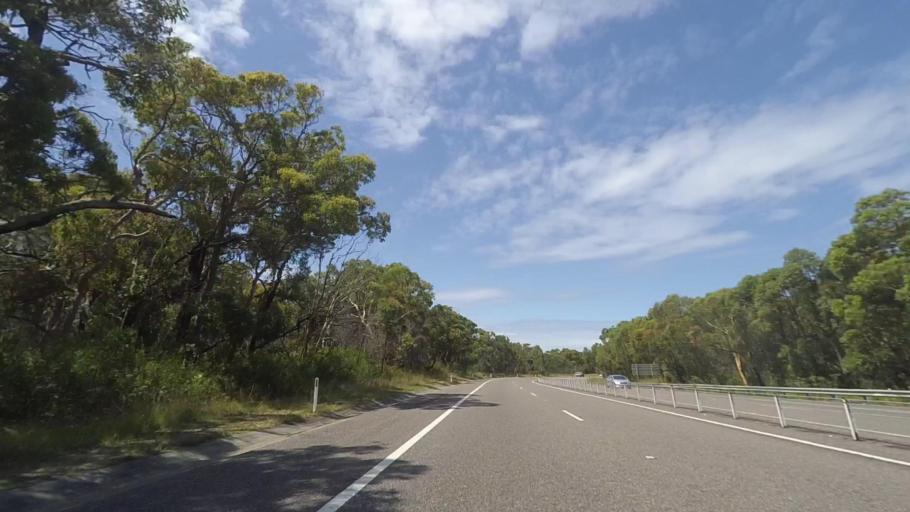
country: AU
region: New South Wales
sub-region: Wyong Shire
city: Kingfisher Shores
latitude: -33.1317
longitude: 151.6168
